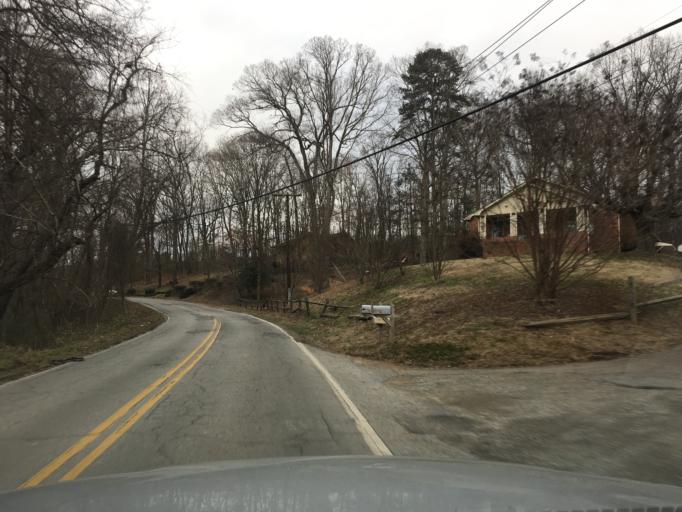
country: US
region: North Carolina
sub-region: Buncombe County
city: Asheville
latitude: 35.5965
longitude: -82.5778
